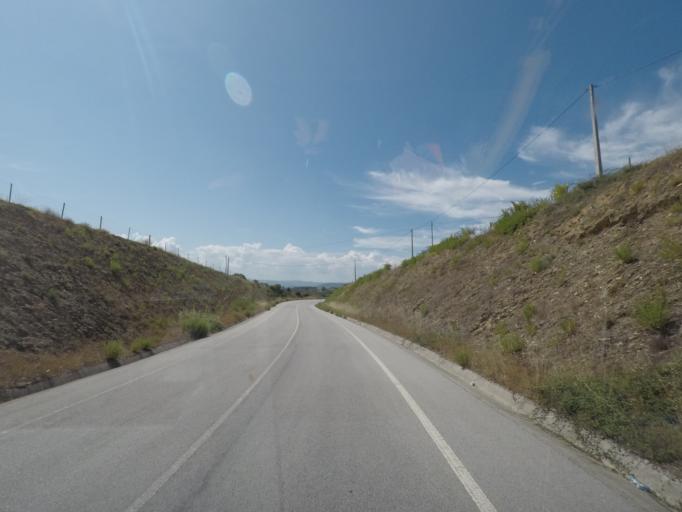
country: PT
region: Vila Real
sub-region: Sabrosa
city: Sabrosa
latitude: 41.2597
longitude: -7.5007
